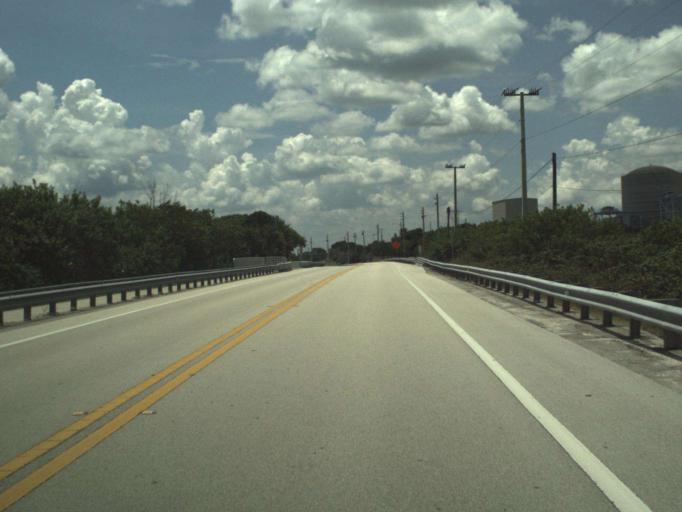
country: US
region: Florida
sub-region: Saint Lucie County
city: Hutchinson Island South
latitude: 27.3554
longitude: -80.2462
